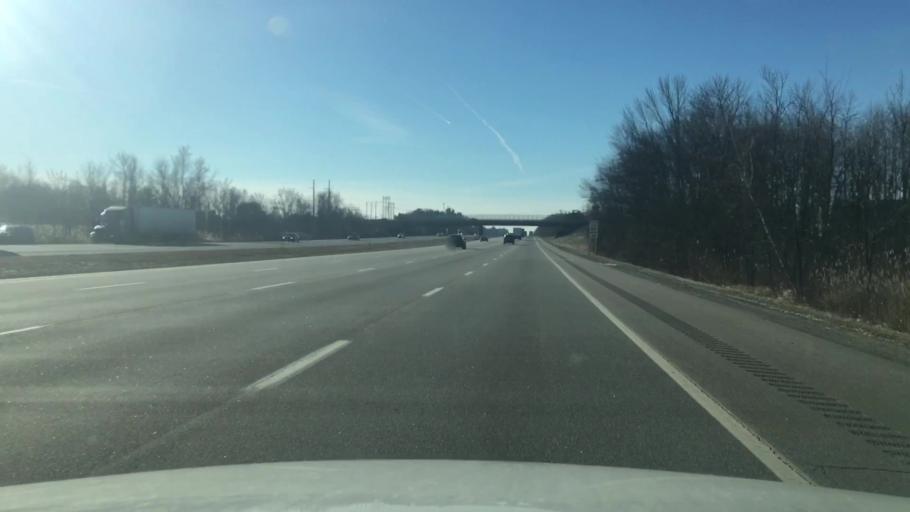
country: US
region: New Hampshire
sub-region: Rockingham County
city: Greenland
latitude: 43.0459
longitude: -70.8148
